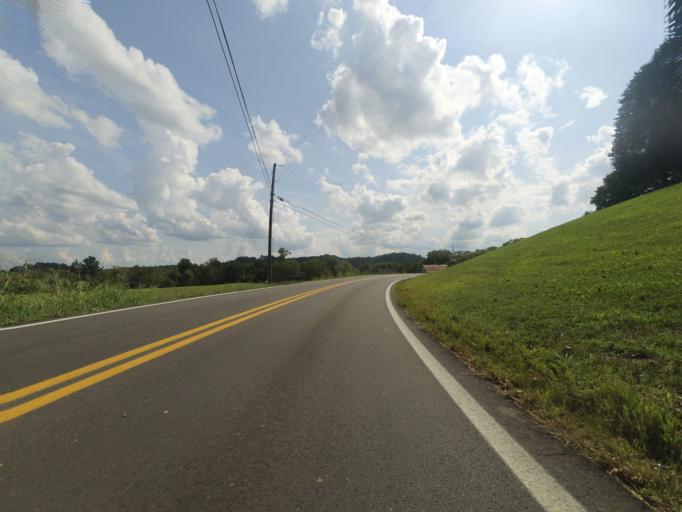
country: US
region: Ohio
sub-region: Lawrence County
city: Burlington
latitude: 38.3743
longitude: -82.5335
